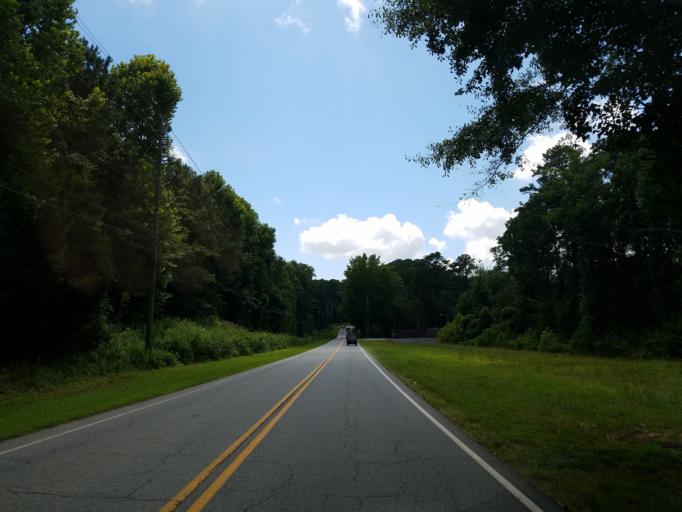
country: US
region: Georgia
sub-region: Fulton County
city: Johns Creek
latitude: 34.0994
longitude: -84.2185
